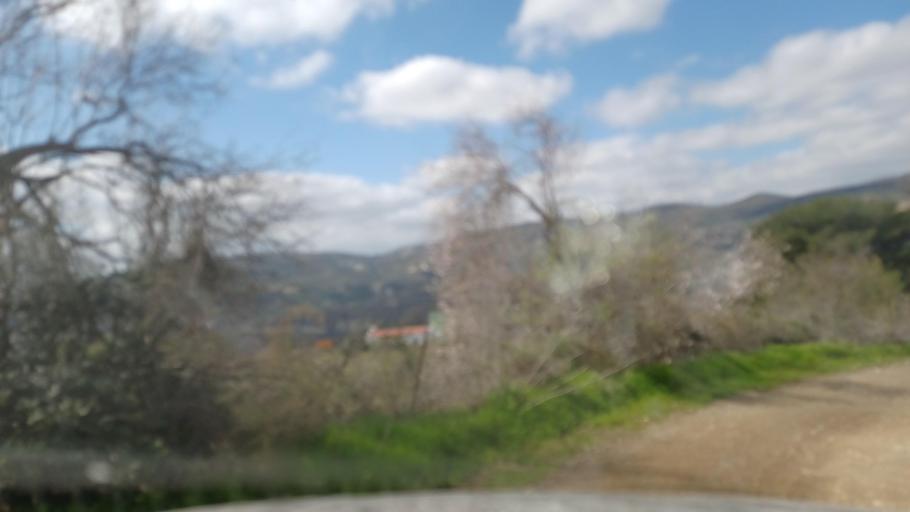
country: CY
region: Limassol
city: Pachna
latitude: 34.8439
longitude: 32.7338
